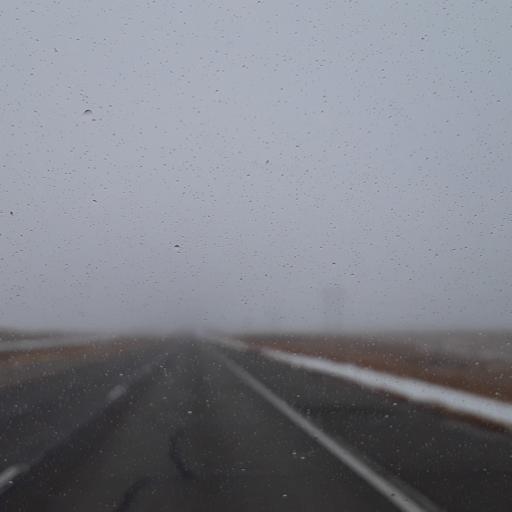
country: US
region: Colorado
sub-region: Logan County
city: Sterling
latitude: 40.7786
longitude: -102.9193
